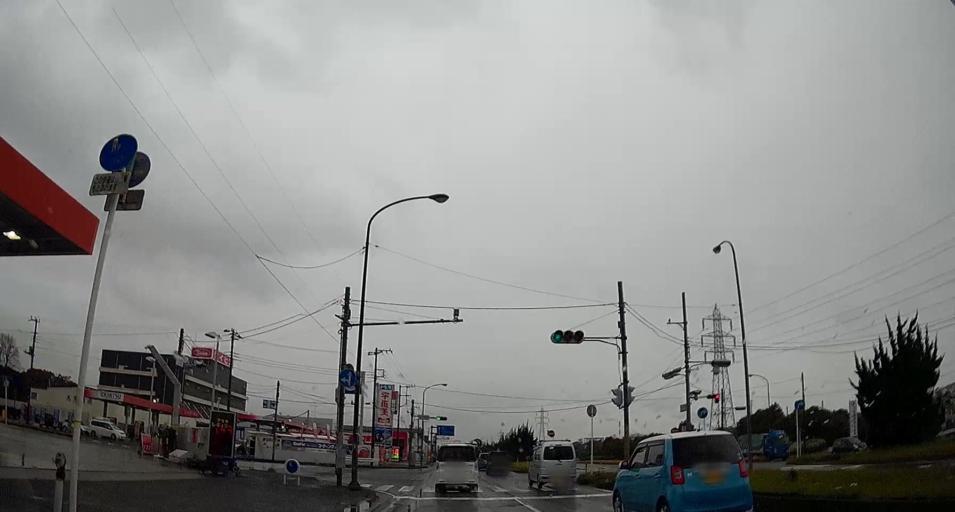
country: JP
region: Chiba
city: Ichihara
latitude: 35.5197
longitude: 140.0617
